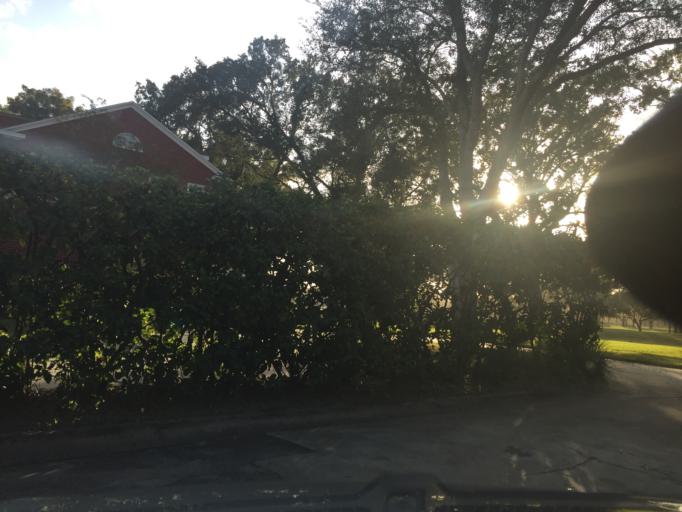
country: US
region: Florida
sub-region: Hillsborough County
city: Tampa
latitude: 27.9316
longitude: -82.4945
